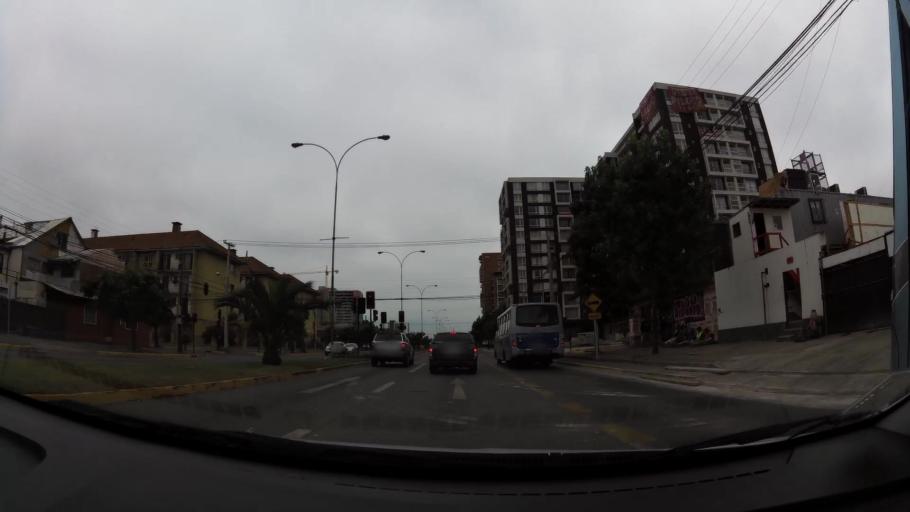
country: CL
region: Biobio
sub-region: Provincia de Concepcion
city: Concepcion
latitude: -36.8167
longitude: -73.0364
